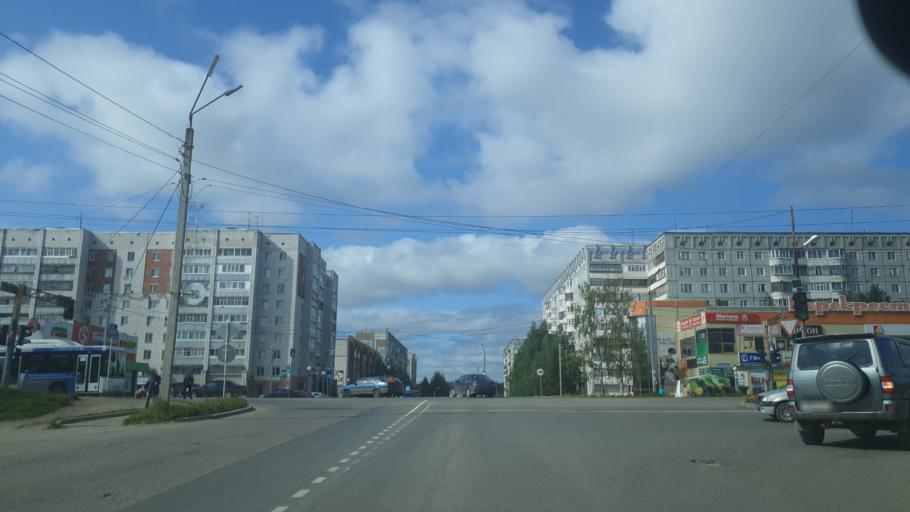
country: RU
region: Komi Republic
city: Ezhva
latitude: 61.7815
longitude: 50.7489
